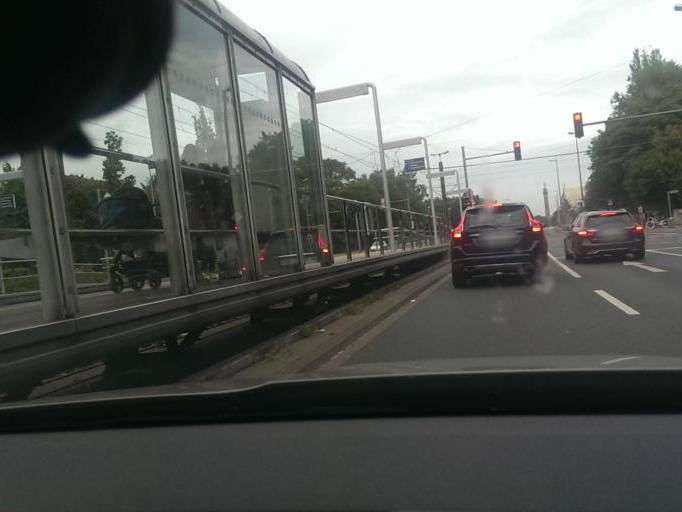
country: DE
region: Lower Saxony
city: Hannover
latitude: 52.3621
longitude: 9.7219
